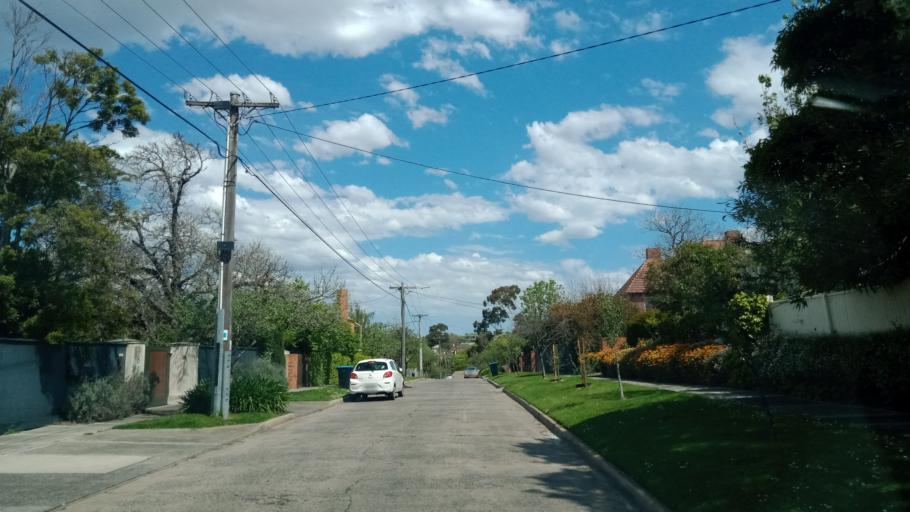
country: AU
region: Victoria
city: Glenferrie
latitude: -37.8469
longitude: 145.0349
